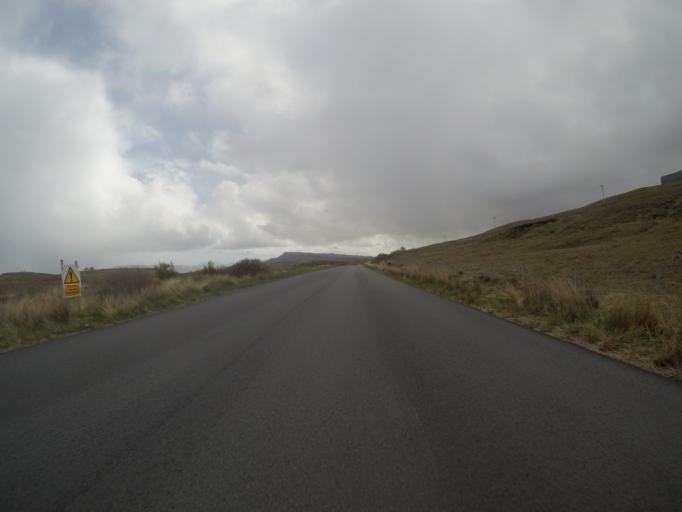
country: GB
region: Scotland
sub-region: Highland
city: Portree
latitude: 57.5075
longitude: -6.1514
